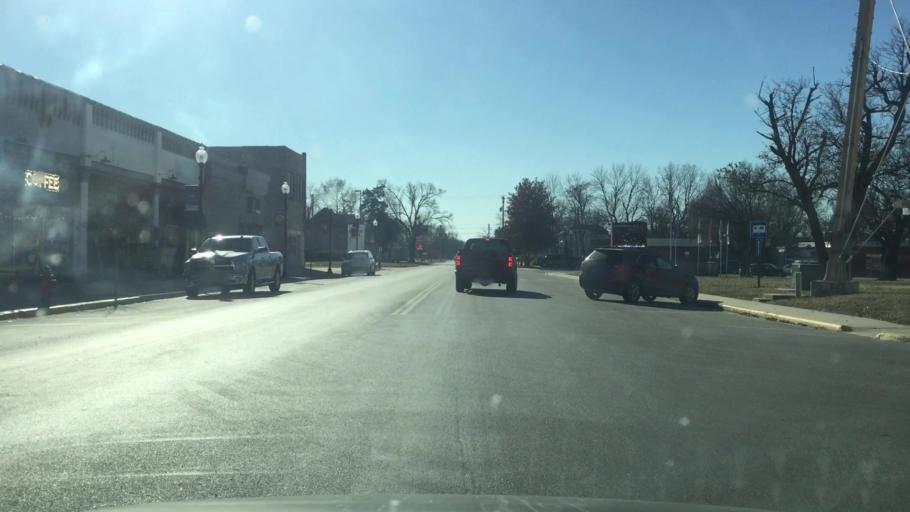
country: US
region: Kansas
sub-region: Allen County
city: Humboldt
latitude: 37.8112
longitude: -95.4355
